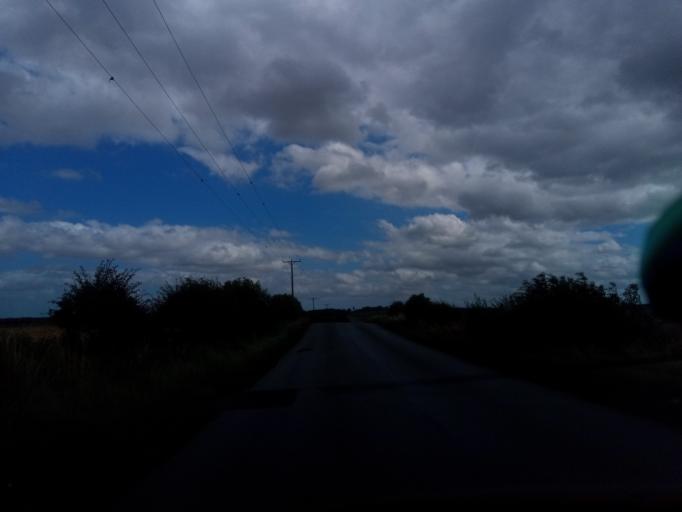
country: GB
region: Scotland
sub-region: The Scottish Borders
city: Kelso
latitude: 55.6281
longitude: -2.3449
